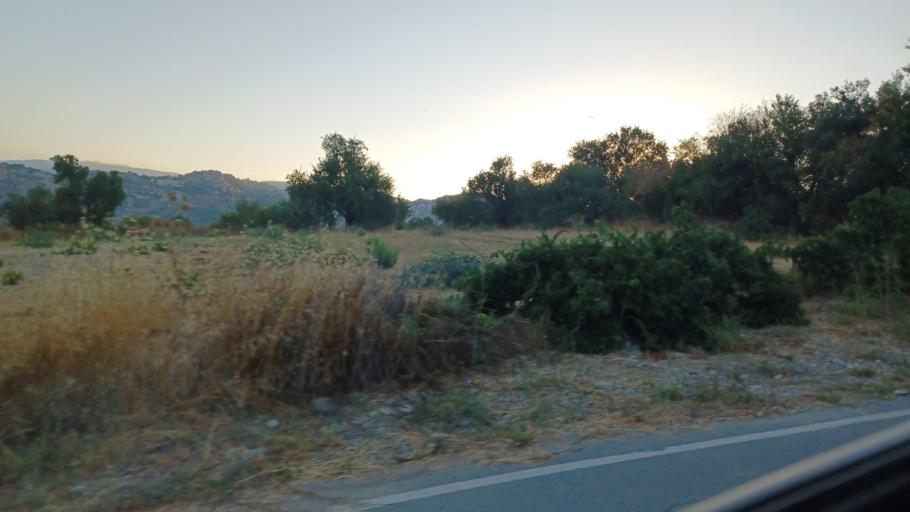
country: CY
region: Pafos
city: Mesogi
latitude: 34.8269
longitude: 32.5783
